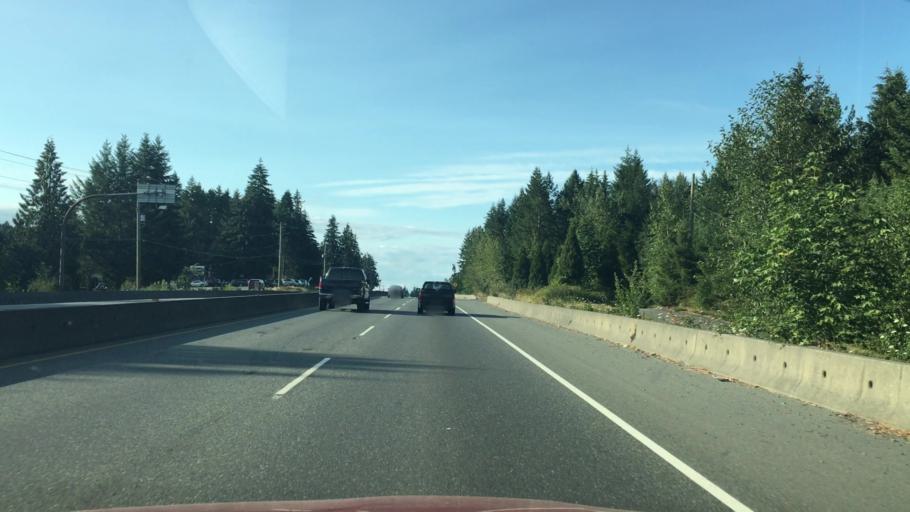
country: CA
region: British Columbia
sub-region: Cowichan Valley Regional District
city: Ladysmith
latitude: 48.9538
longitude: -123.7783
